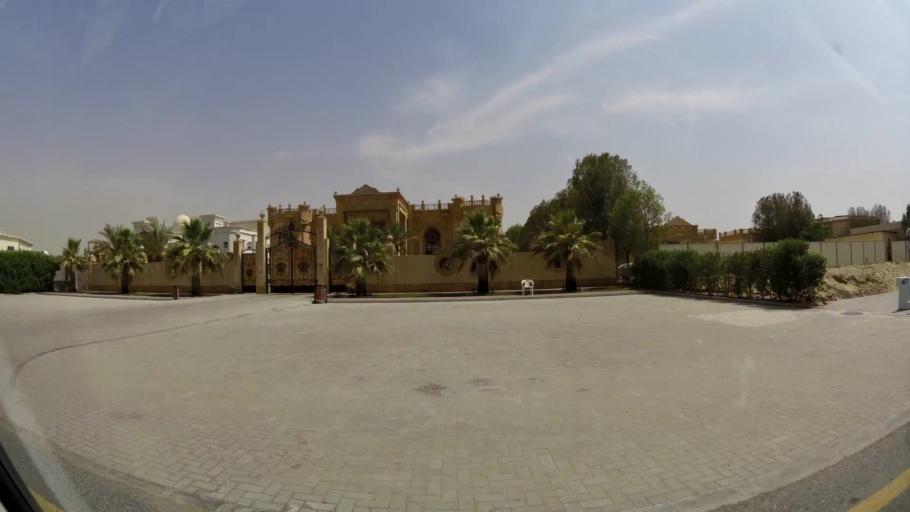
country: AE
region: Ash Shariqah
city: Sharjah
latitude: 25.2502
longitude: 55.4777
